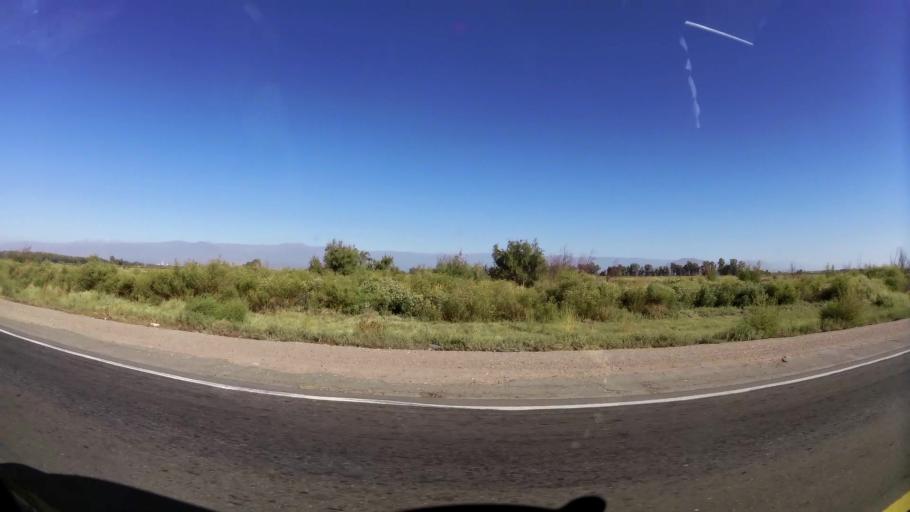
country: AR
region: Mendoza
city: General Lavalle
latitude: -32.7153
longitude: -68.6797
